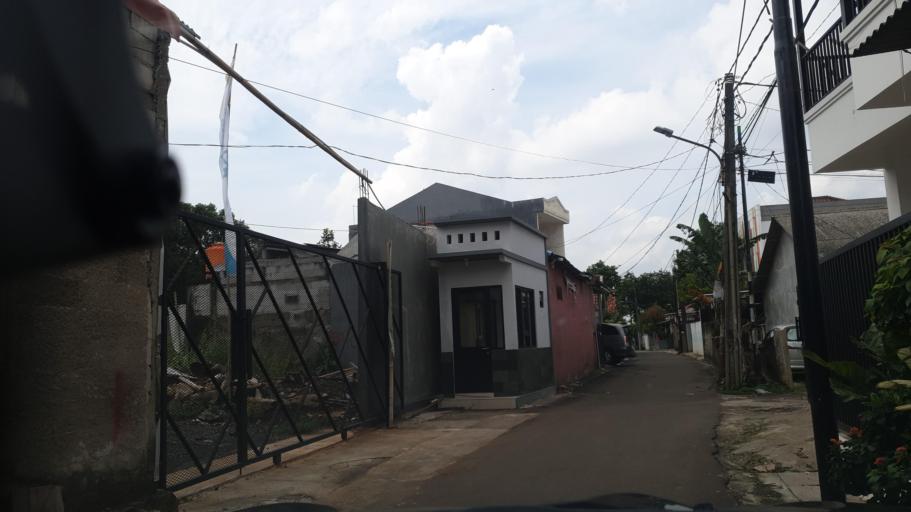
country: ID
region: West Java
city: Pamulang
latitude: -6.3362
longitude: 106.7730
